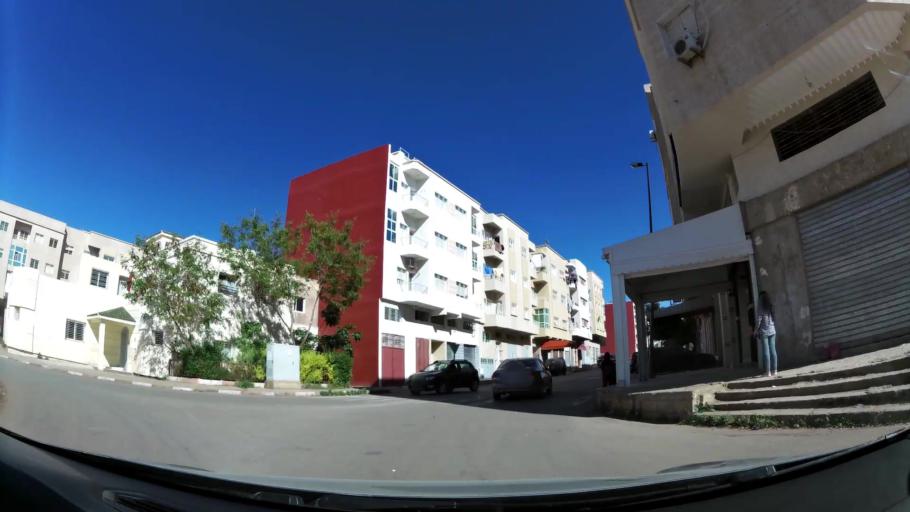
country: MA
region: Fes-Boulemane
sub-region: Fes
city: Fes
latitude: 34.0160
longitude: -4.9635
